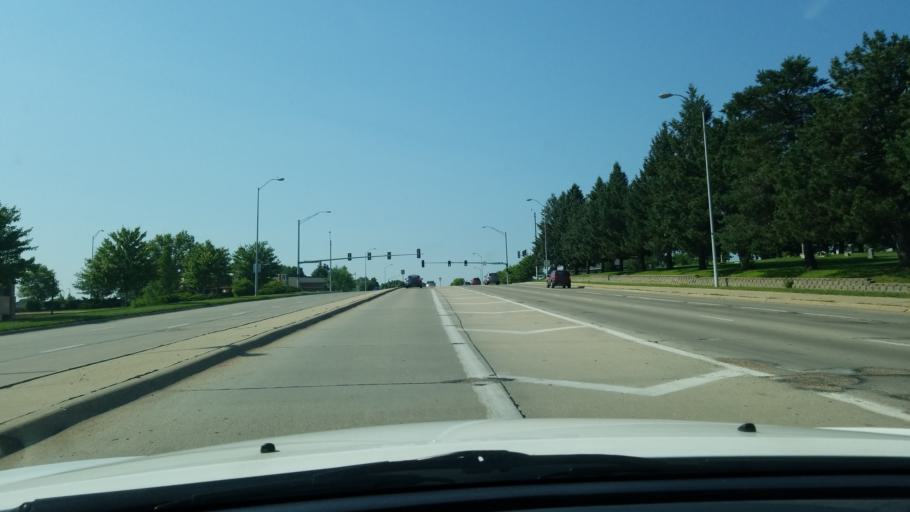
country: US
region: Nebraska
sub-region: Lancaster County
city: Lincoln
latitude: 40.7710
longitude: -96.6252
